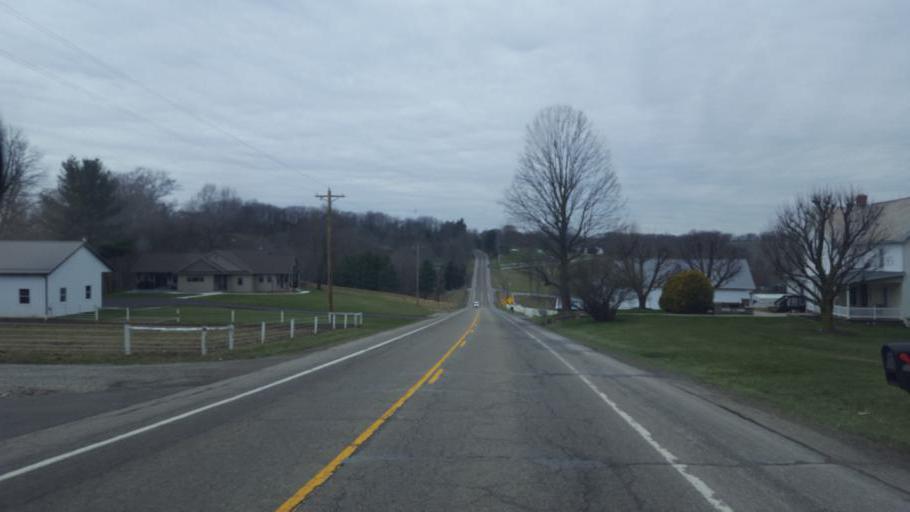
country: US
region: Ohio
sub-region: Tuscarawas County
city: Sugarcreek
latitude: 40.6055
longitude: -81.7273
